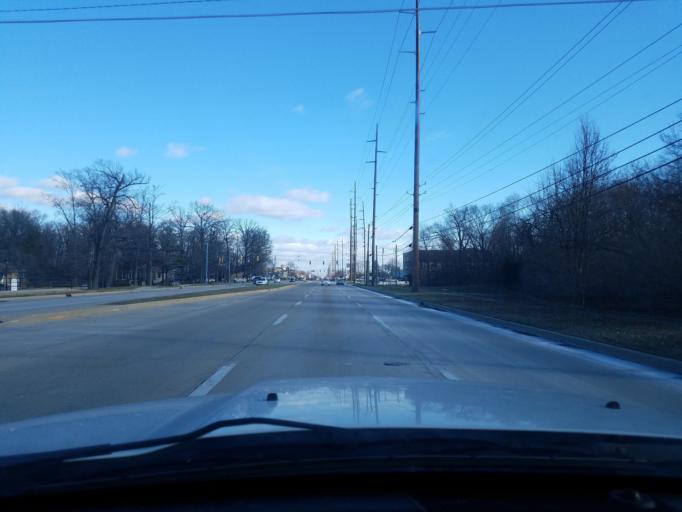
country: US
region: Indiana
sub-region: Boone County
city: Zionsville
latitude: 39.9116
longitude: -86.2309
